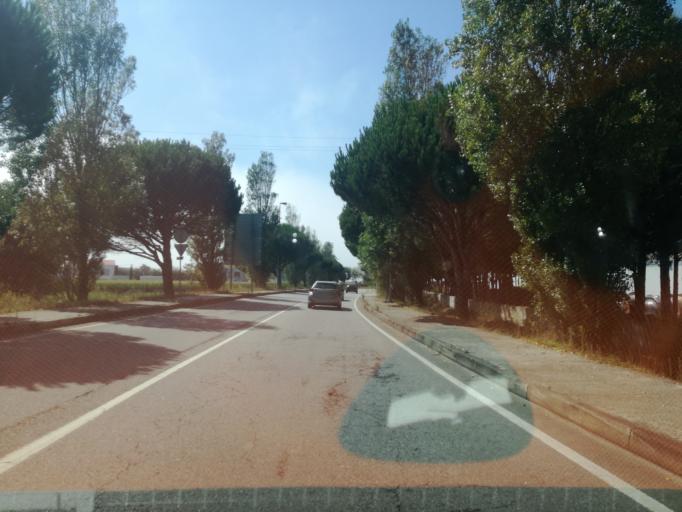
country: PT
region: Braga
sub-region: Esposende
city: Esposende
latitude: 41.5250
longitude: -8.7735
